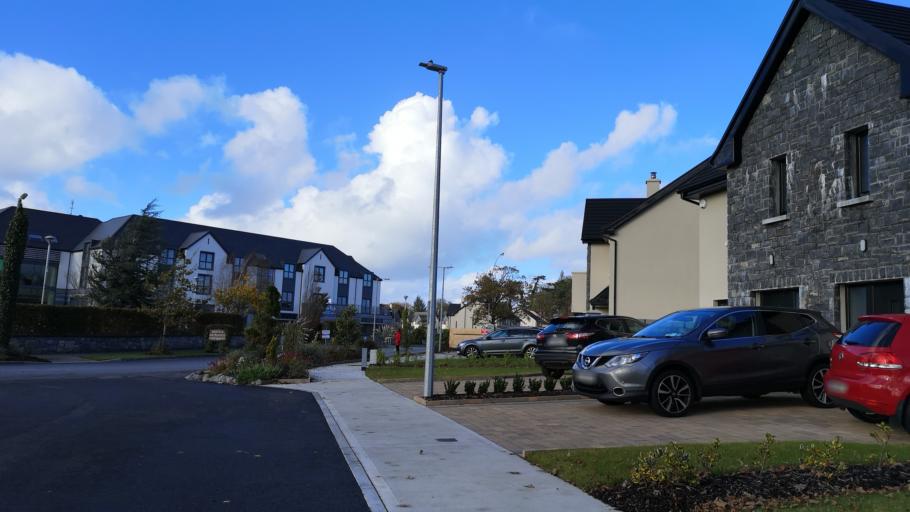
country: IE
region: Connaught
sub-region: County Galway
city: Athenry
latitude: 53.2999
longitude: -8.7604
